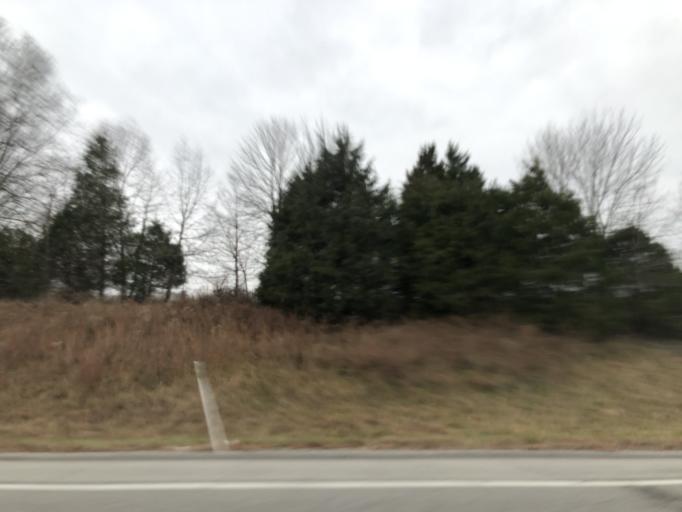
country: US
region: Illinois
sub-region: Johnson County
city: Goreville
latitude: 37.5300
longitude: -88.9215
